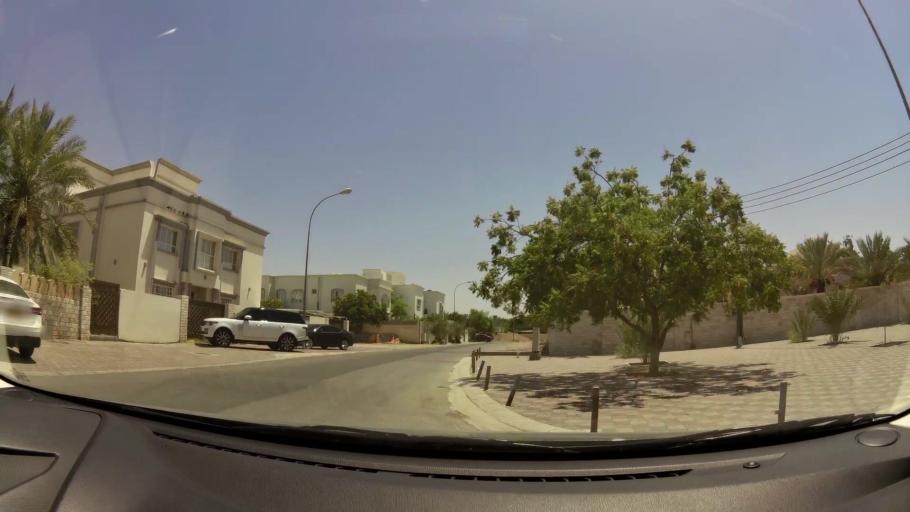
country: OM
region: Muhafazat Masqat
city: As Sib al Jadidah
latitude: 23.6197
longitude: 58.2333
